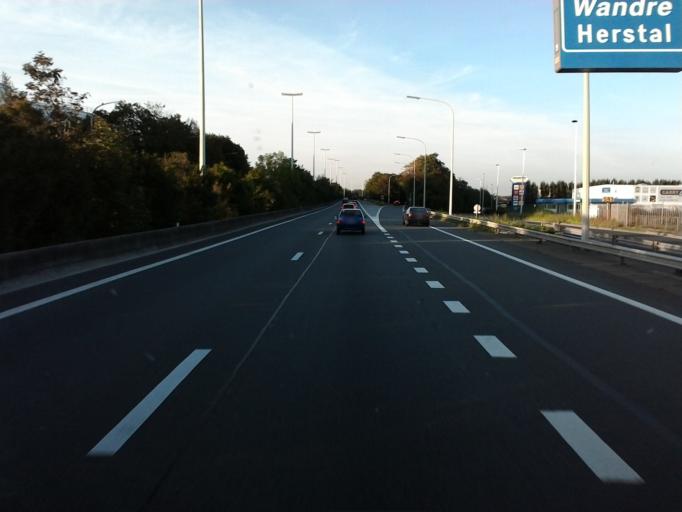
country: BE
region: Wallonia
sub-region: Province de Liege
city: Herstal
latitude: 50.6683
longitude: 5.6466
